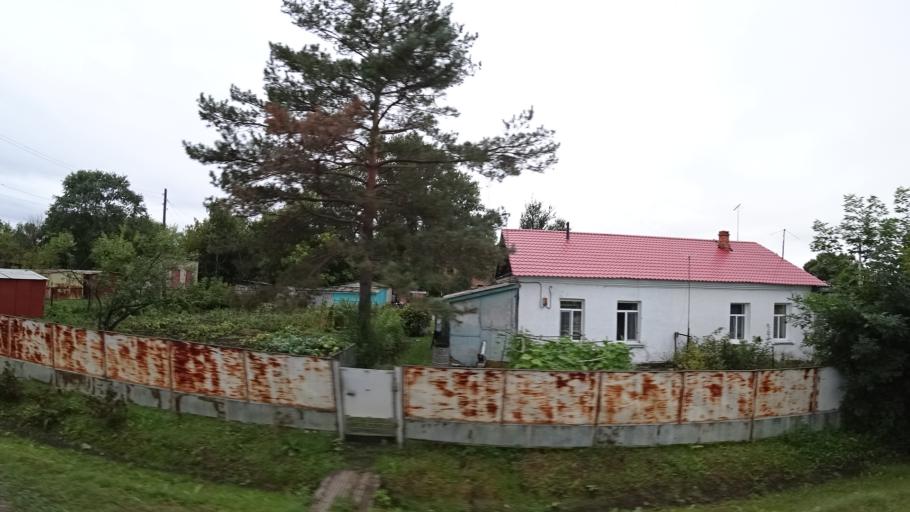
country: RU
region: Primorskiy
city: Chernigovka
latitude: 44.3340
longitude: 132.5316
